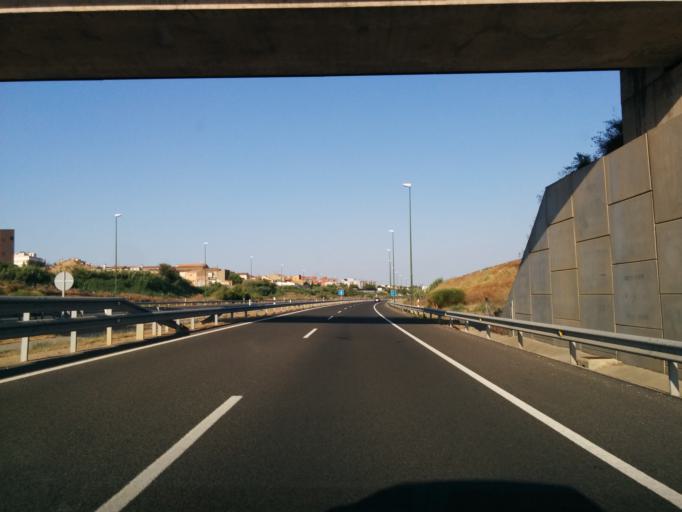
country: ES
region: Aragon
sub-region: Provincia de Zaragoza
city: Zaragoza
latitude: 41.6653
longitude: -0.8332
